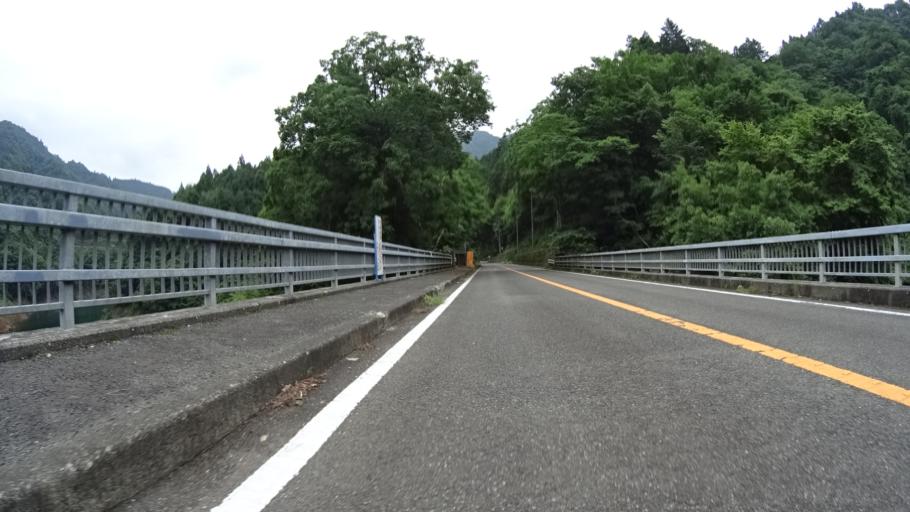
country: JP
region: Kanagawa
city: Hadano
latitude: 35.5040
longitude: 139.2296
